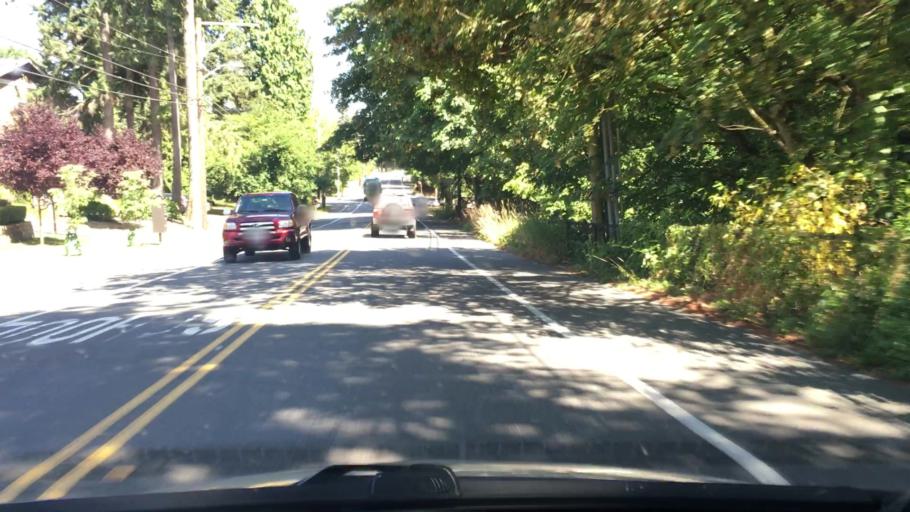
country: US
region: Washington
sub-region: King County
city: Kingsgate
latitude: 47.6865
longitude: -122.1646
